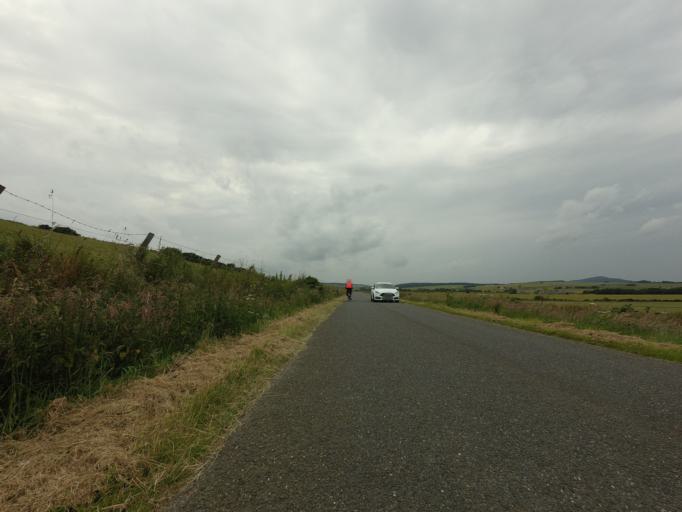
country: GB
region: Scotland
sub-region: Aberdeenshire
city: Portsoy
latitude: 57.6669
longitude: -2.7275
